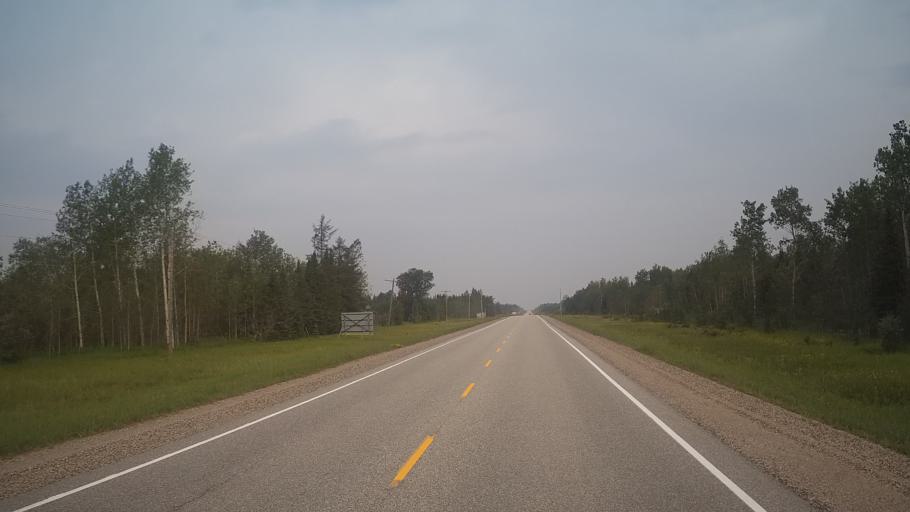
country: CA
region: Ontario
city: Hearst
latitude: 49.7205
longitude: -83.8547
